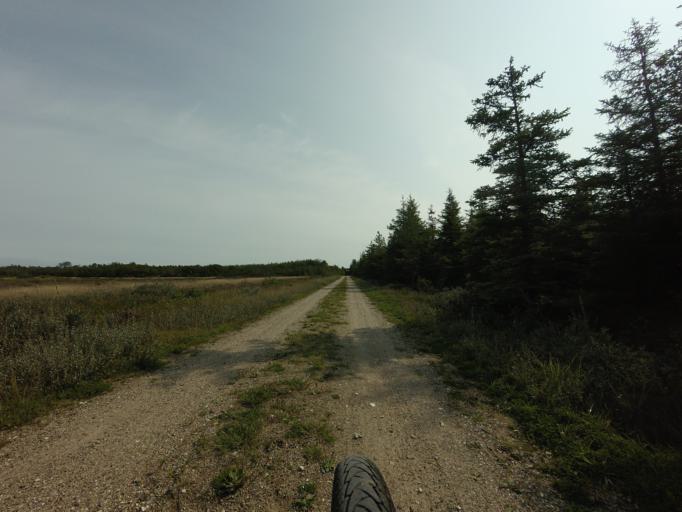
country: DK
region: North Denmark
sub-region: Frederikshavn Kommune
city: Strandby
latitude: 57.6416
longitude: 10.4186
